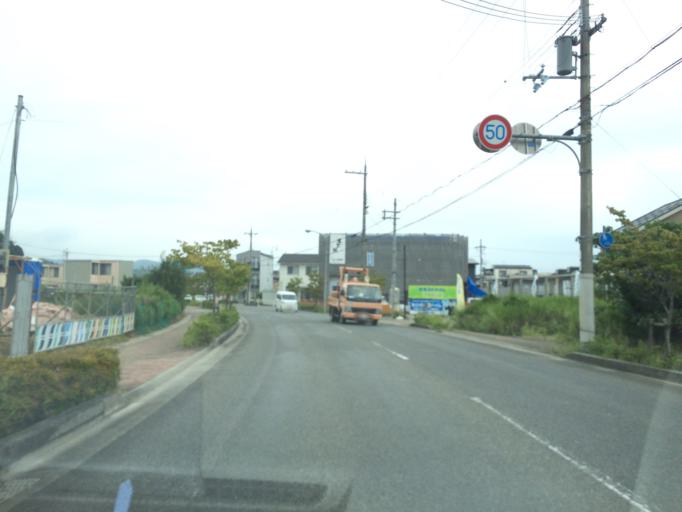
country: JP
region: Hyogo
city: Toyooka
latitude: 35.5443
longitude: 134.8101
